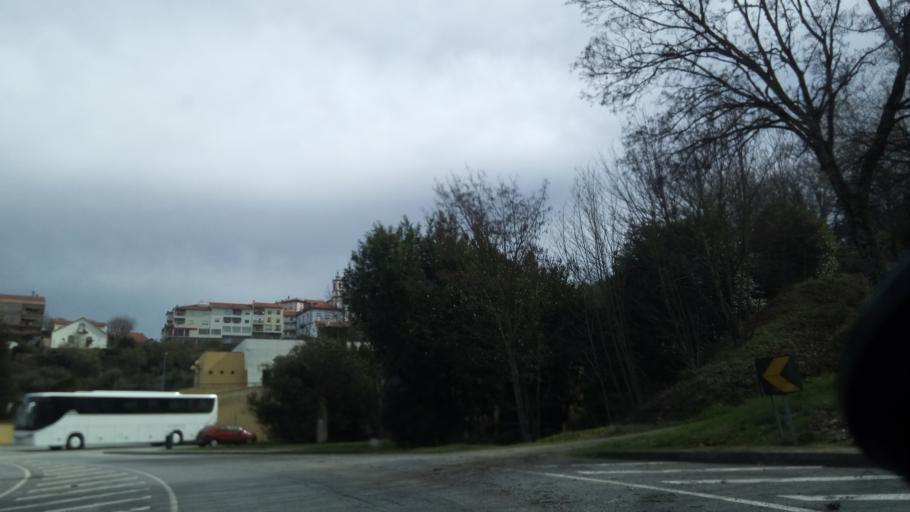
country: PT
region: Guarda
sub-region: Seia
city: Seia
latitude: 40.4199
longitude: -7.7075
